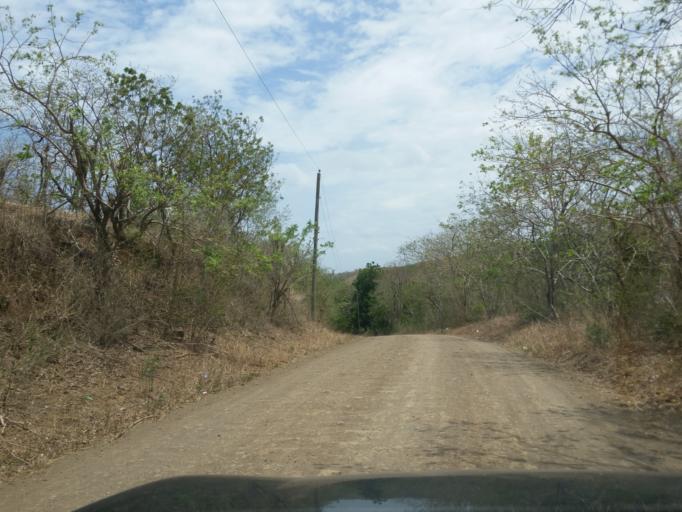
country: NI
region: Rivas
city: Tola
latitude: 11.5256
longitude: -86.0627
